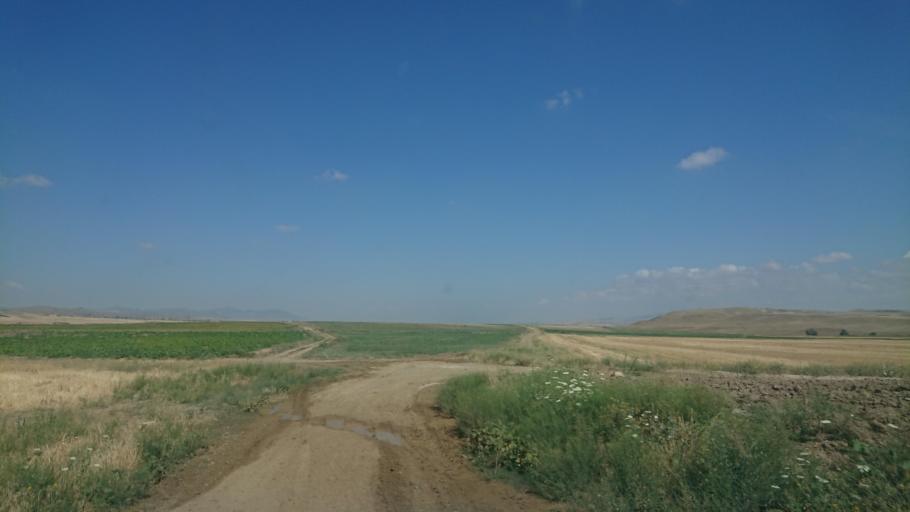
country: TR
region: Aksaray
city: Sariyahsi
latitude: 38.9634
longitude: 33.9269
